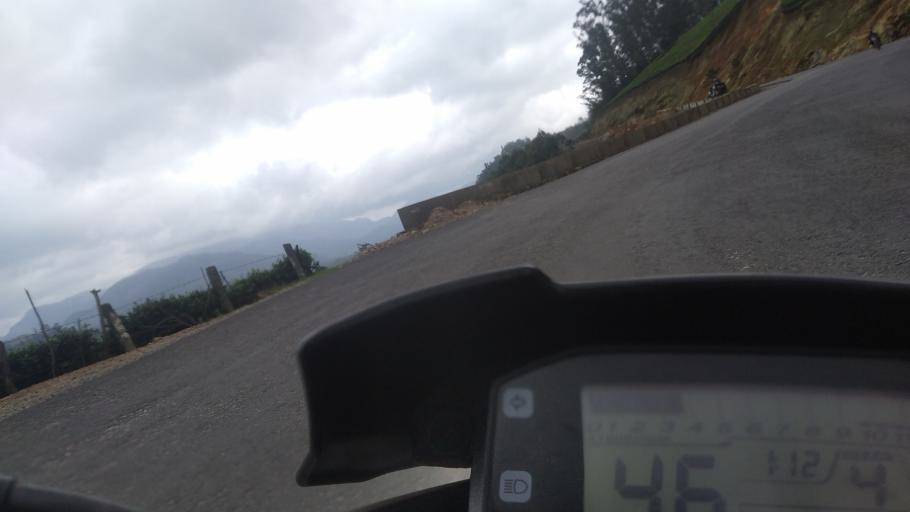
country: IN
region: Kerala
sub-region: Idukki
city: Munnar
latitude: 10.0815
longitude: 77.0782
